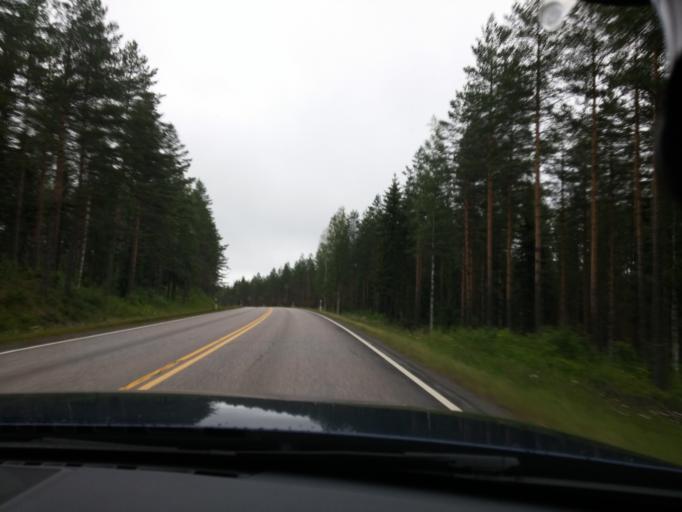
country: FI
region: Pirkanmaa
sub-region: Ylae-Pirkanmaa
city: Vilppula
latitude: 61.9261
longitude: 24.5418
